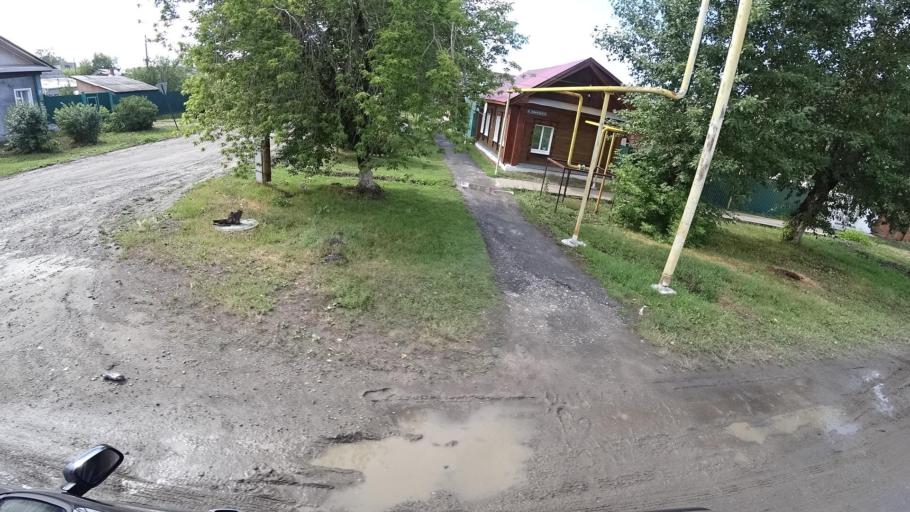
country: RU
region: Sverdlovsk
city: Kamyshlov
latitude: 56.8401
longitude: 62.7214
